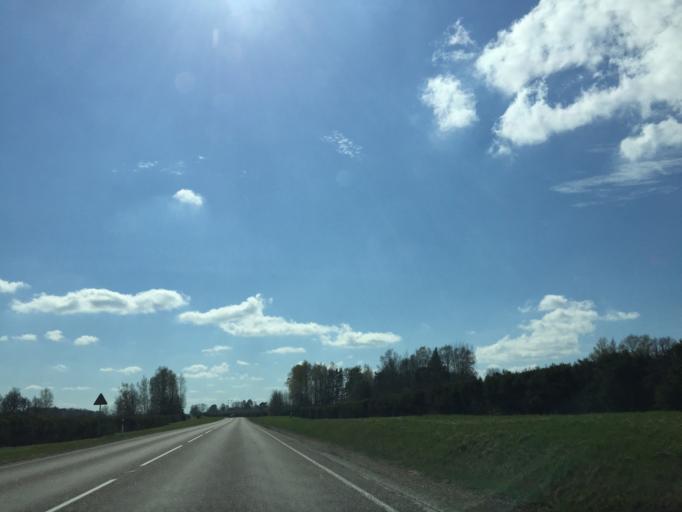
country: EE
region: Valgamaa
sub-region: Torva linn
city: Torva
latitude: 58.0438
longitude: 26.1905
